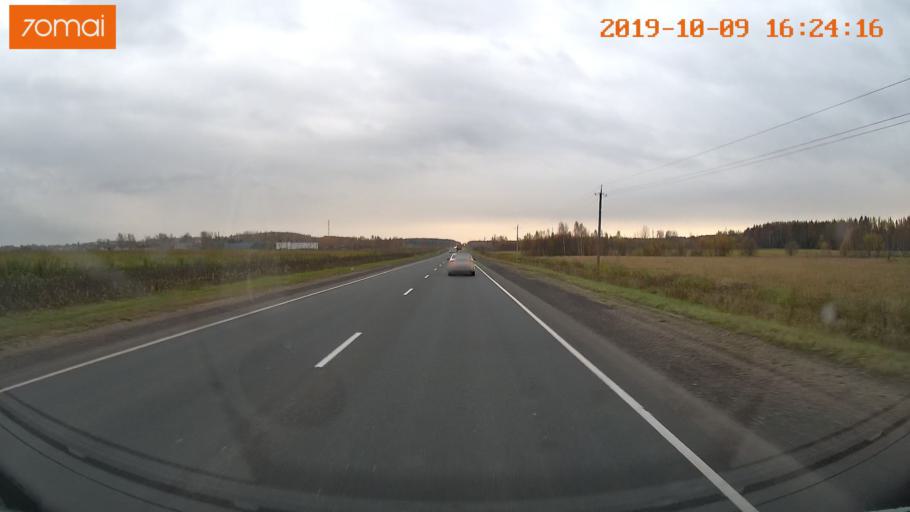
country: RU
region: Kostroma
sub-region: Kostromskoy Rayon
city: Kostroma
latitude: 57.6543
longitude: 40.9086
